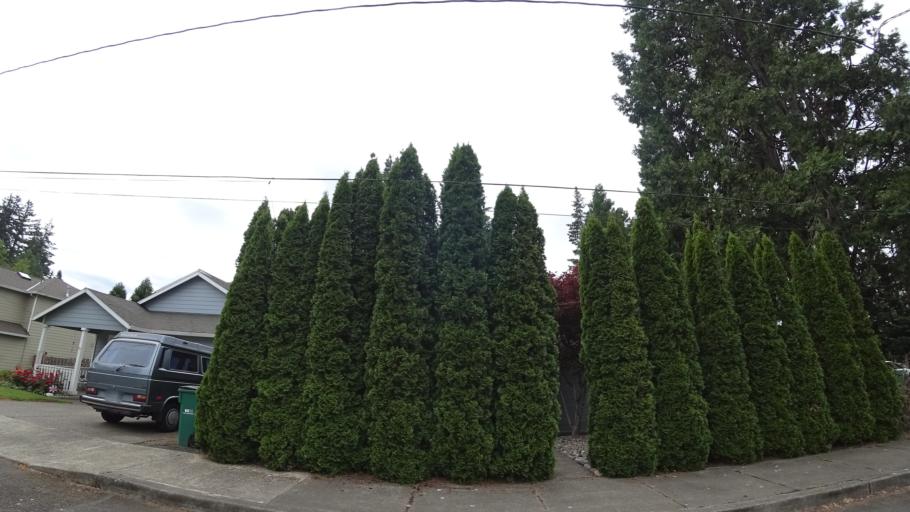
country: US
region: Oregon
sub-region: Washington County
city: Garden Home-Whitford
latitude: 45.4633
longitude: -122.7558
